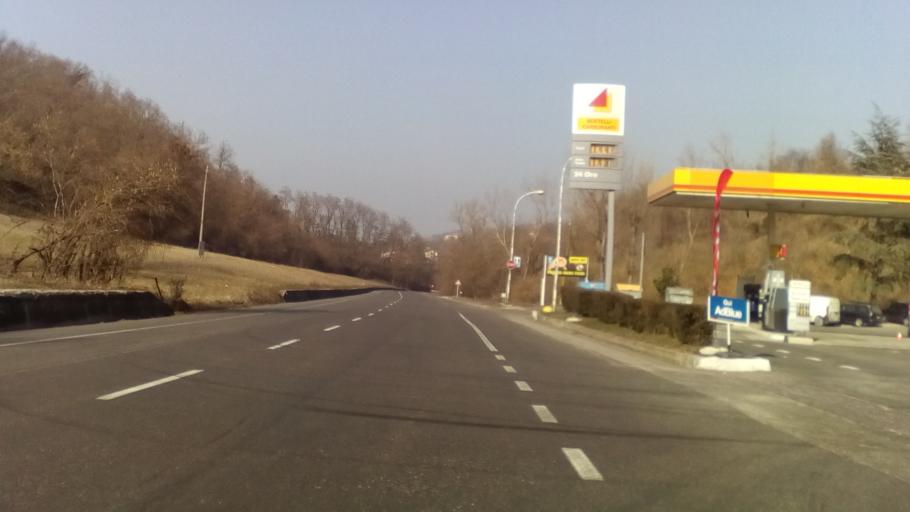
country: IT
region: Emilia-Romagna
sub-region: Provincia di Modena
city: Sant'Antonio
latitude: 44.4173
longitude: 10.8470
